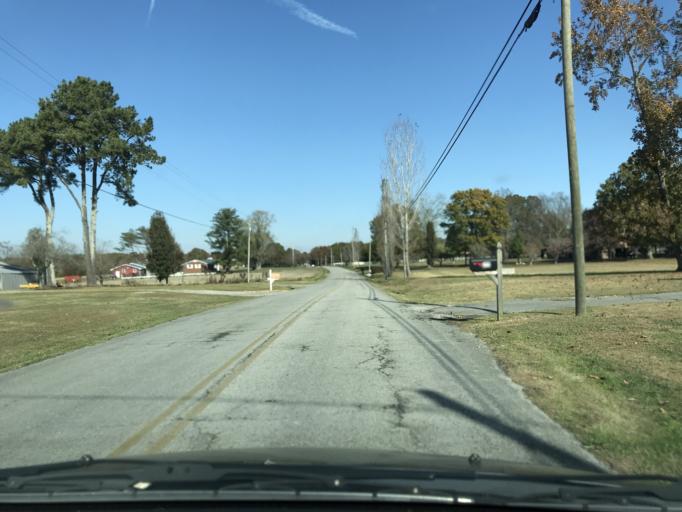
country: US
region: Tennessee
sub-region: Coffee County
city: Tullahoma
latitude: 35.3908
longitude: -86.1641
